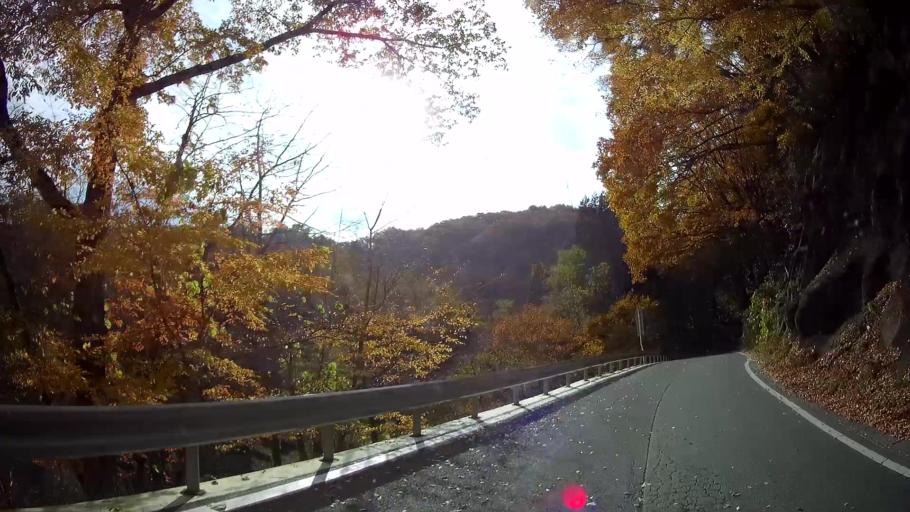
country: JP
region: Gunma
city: Nakanojomachi
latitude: 36.6169
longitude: 138.6389
